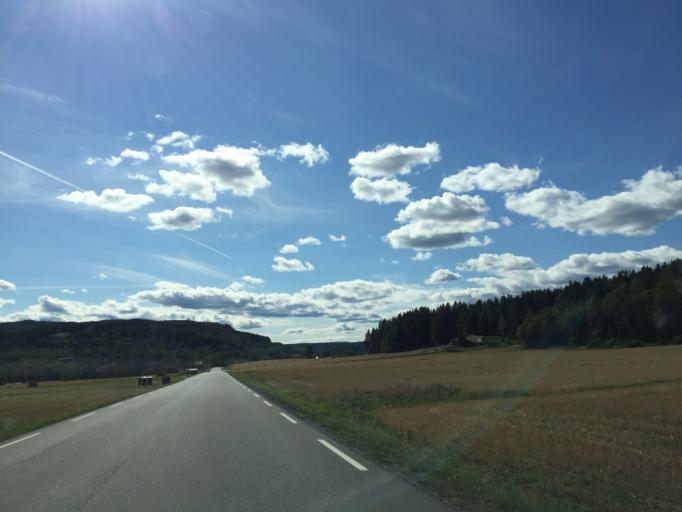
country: NO
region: Buskerud
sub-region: Ovre Eiker
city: Hokksund
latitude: 59.7043
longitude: 9.8552
